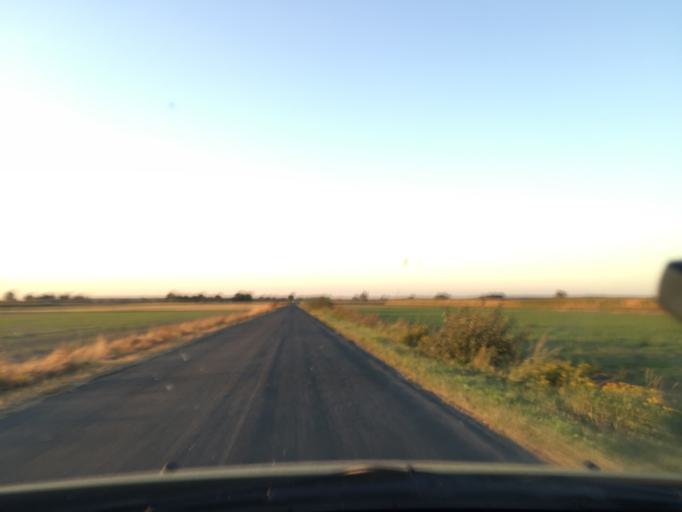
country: PL
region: Greater Poland Voivodeship
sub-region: Powiat jarocinski
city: Golina
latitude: 51.8826
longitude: 17.5346
